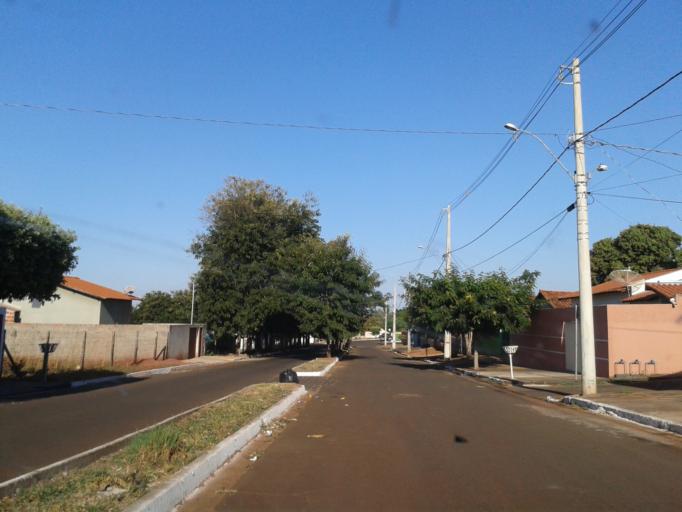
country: BR
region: Minas Gerais
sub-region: Santa Vitoria
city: Santa Vitoria
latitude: -18.8316
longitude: -50.1375
